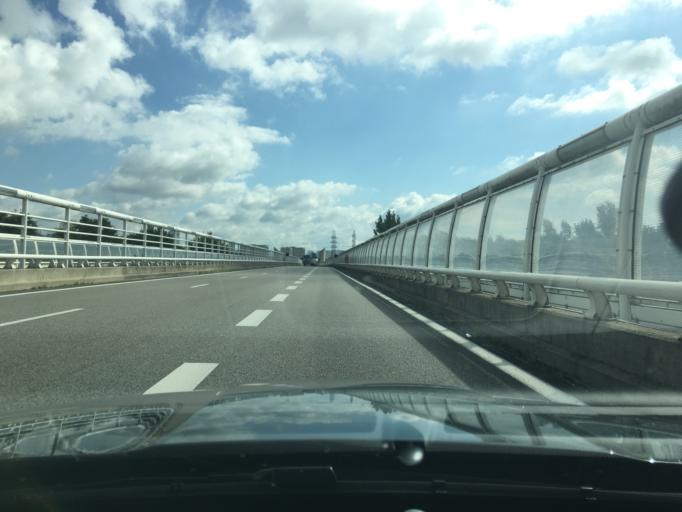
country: FR
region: Ile-de-France
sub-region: Departement des Yvelines
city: Carrieres-sur-Seine
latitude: 48.9076
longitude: 2.1919
